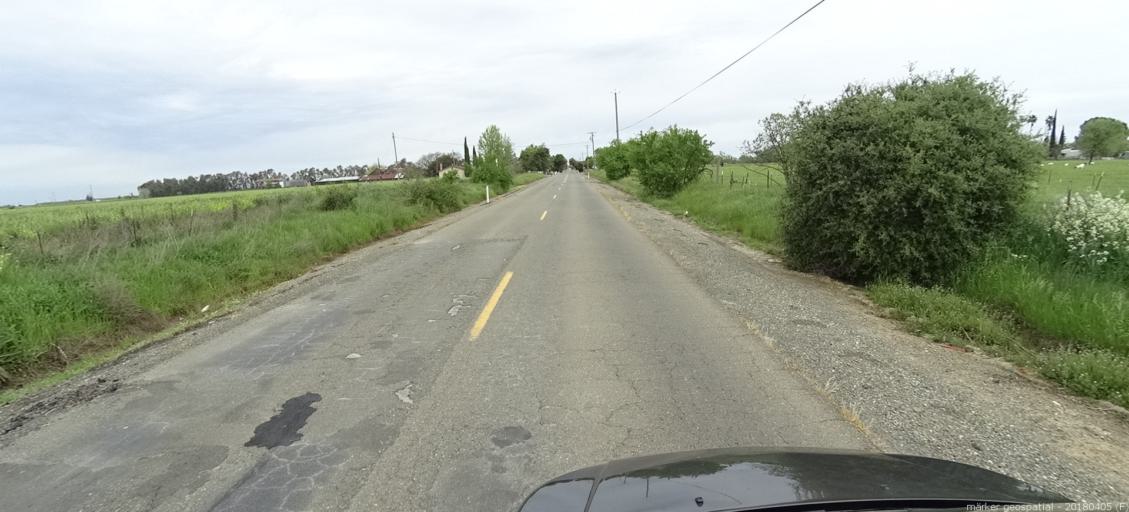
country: US
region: California
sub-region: Sacramento County
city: Galt
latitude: 38.2814
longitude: -121.3374
